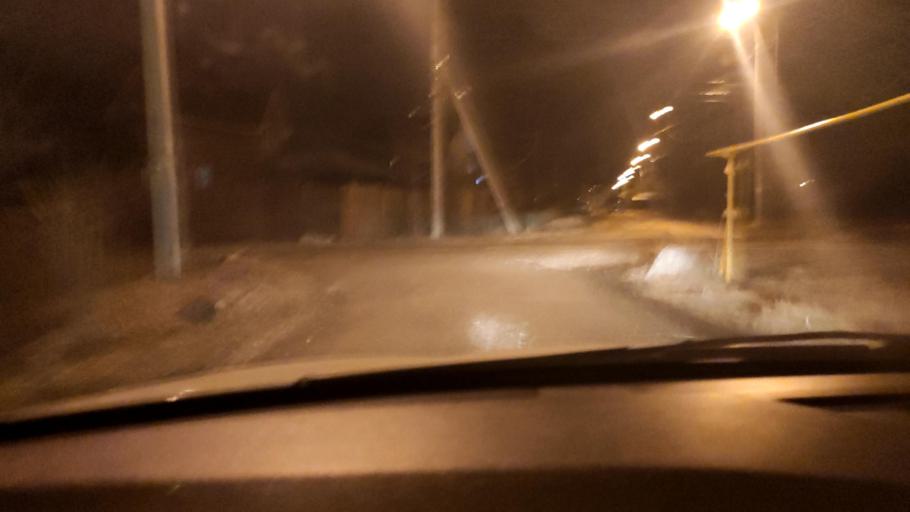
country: RU
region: Perm
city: Perm
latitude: 58.0541
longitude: 56.3635
